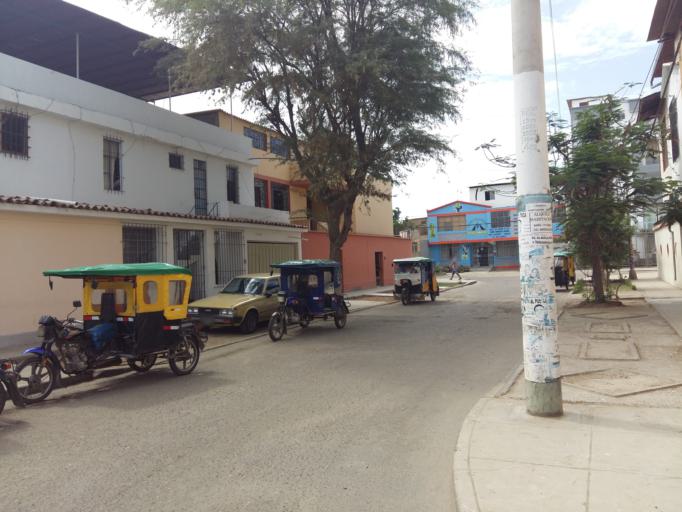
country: PE
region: Piura
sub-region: Provincia de Piura
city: Piura
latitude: -5.1883
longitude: -80.6211
